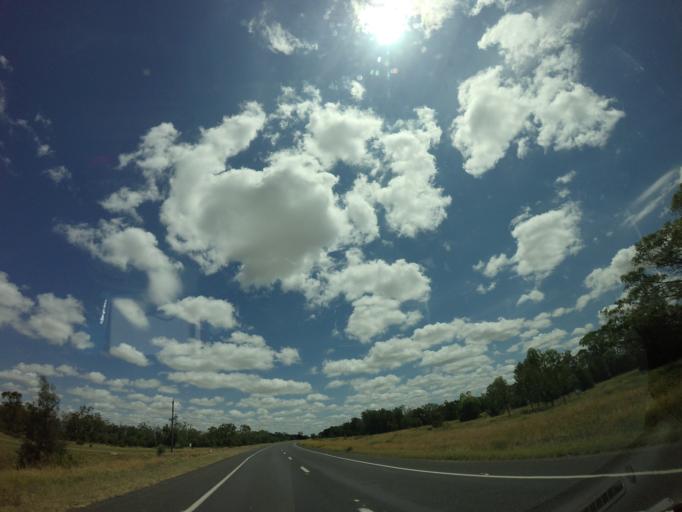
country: AU
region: New South Wales
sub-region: Moree Plains
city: Moree
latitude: -29.1762
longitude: 150.0097
